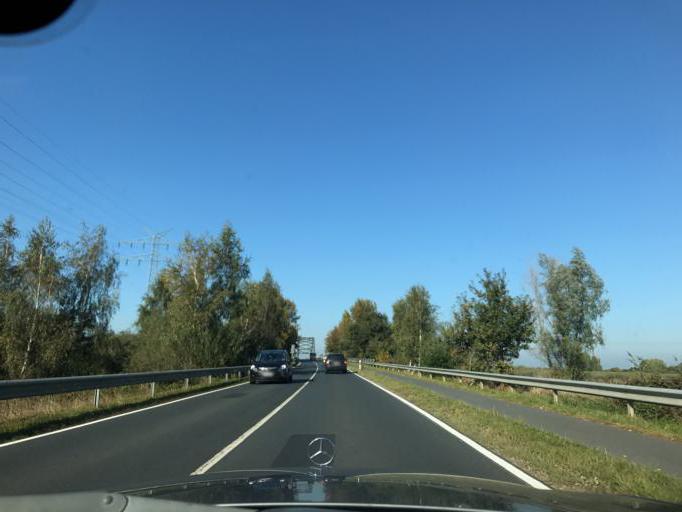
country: DE
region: Lower Saxony
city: Papenburg
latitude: 53.1001
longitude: 7.3539
